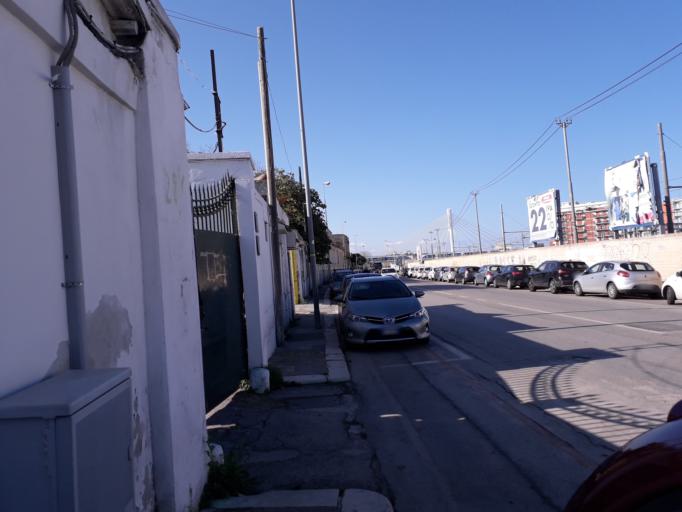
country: IT
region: Apulia
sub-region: Provincia di Bari
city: Bari
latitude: 41.1164
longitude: 16.8554
